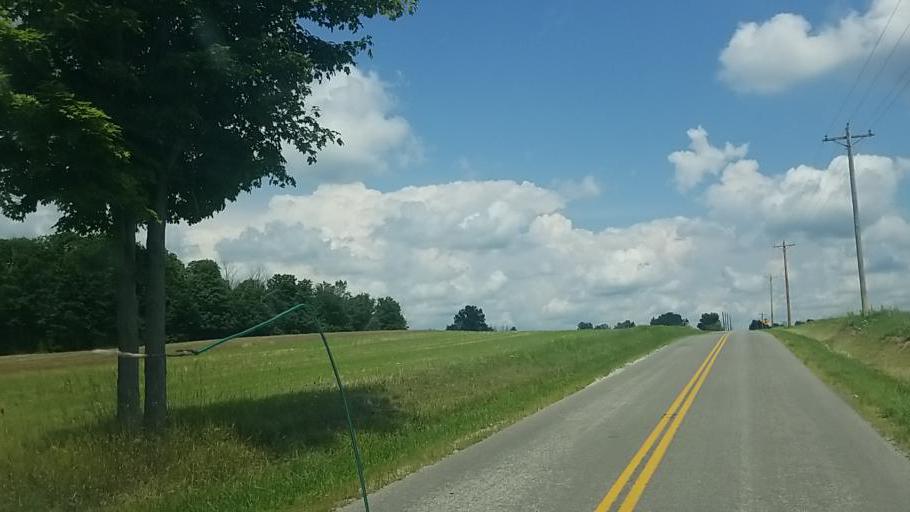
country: US
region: Ohio
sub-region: Medina County
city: Lodi
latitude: 41.0234
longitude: -82.0545
